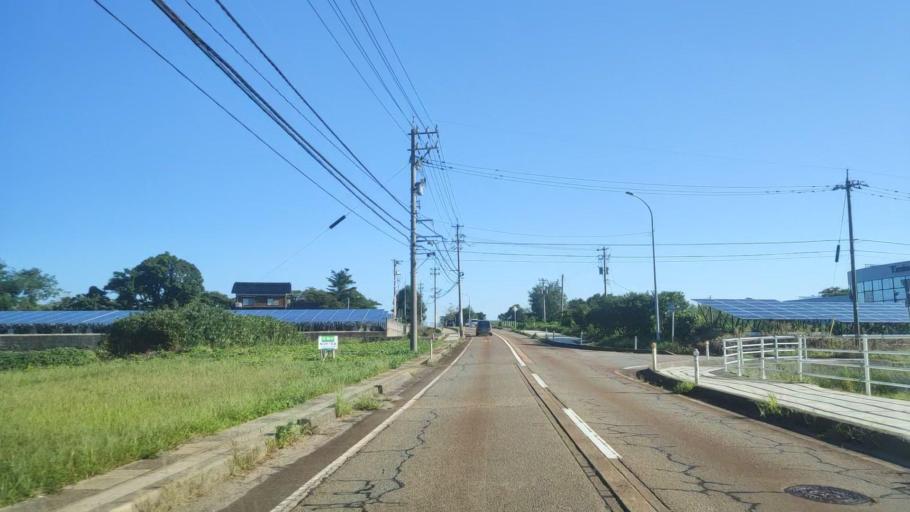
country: JP
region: Ishikawa
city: Hakui
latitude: 36.8156
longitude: 136.7570
